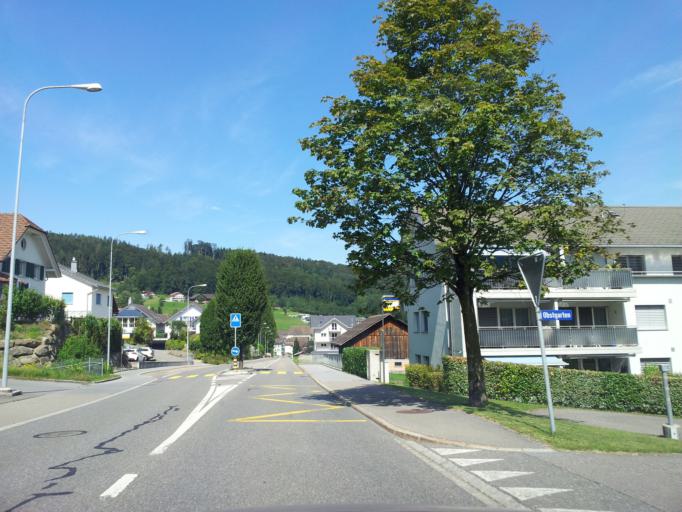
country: CH
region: Schwyz
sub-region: Bezirk March
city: Tuggen
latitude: 47.1983
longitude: 8.9386
